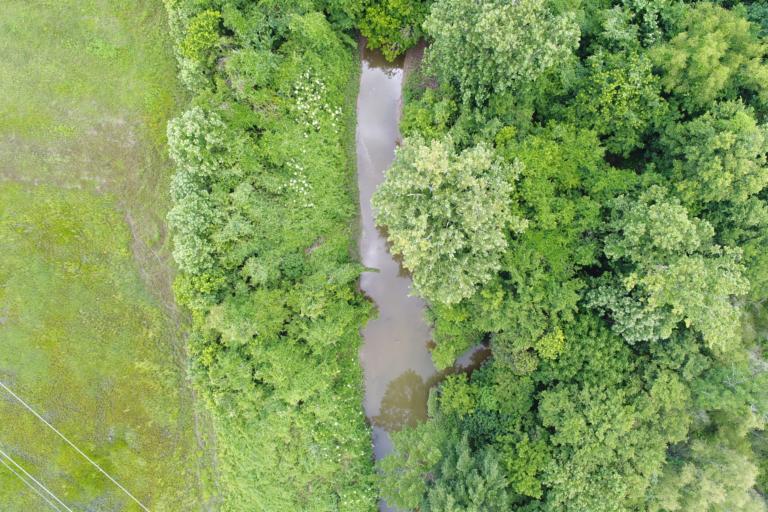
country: US
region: Mississippi
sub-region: De Soto County
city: Walls
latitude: 34.9189
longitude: -90.1877
